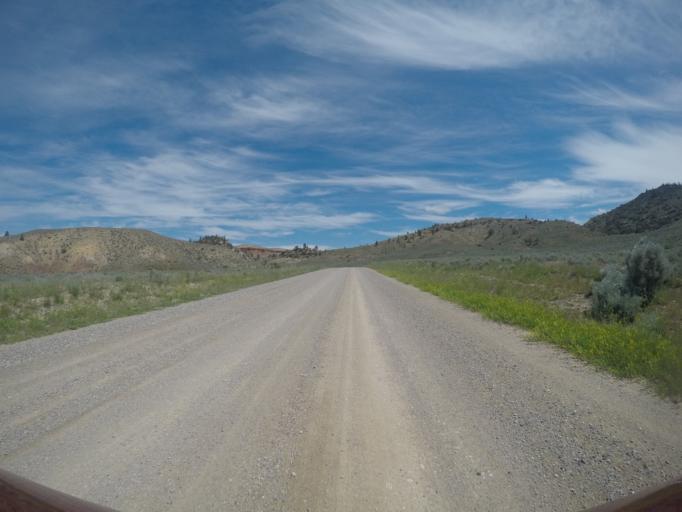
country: US
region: Montana
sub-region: Carbon County
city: Red Lodge
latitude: 45.2059
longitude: -108.8123
